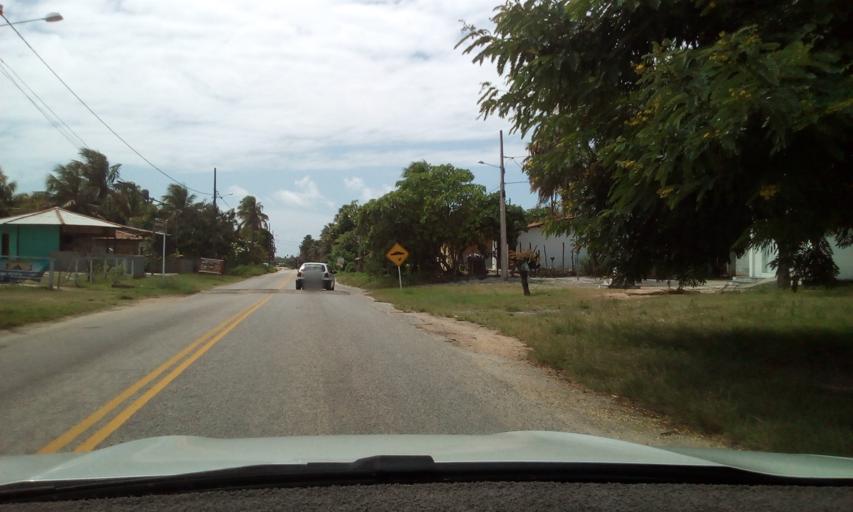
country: BR
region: Paraiba
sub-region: Rio Tinto
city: Rio Tinto
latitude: -6.7186
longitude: -34.9471
